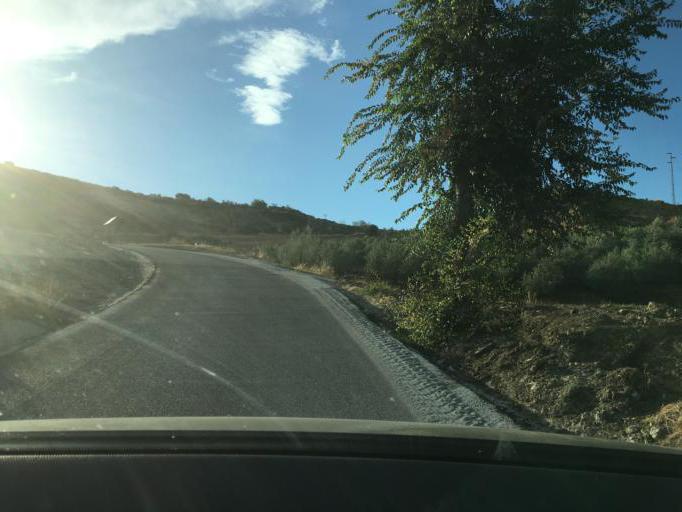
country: ES
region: Andalusia
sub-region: Provincia de Granada
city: Beas de Granada
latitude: 37.2143
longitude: -3.4802
